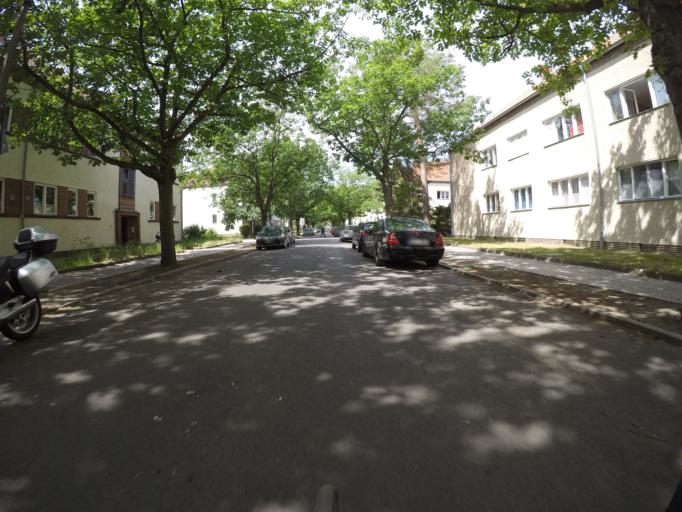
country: DE
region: Berlin
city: Berlin Koepenick
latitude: 52.4623
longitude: 13.5888
